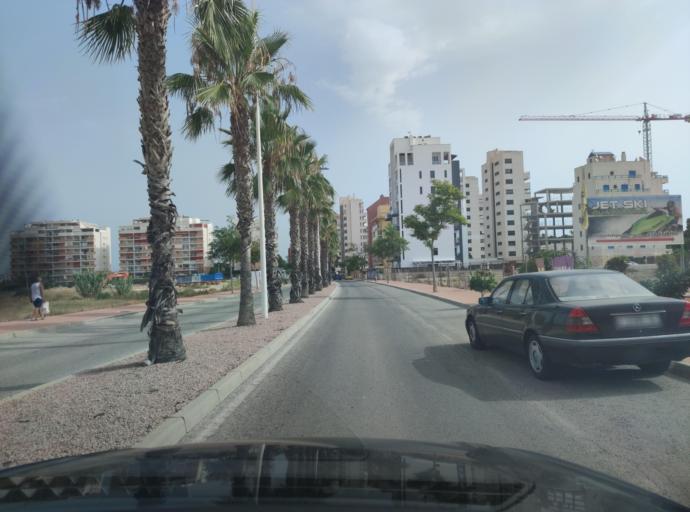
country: ES
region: Valencia
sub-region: Provincia de Alicante
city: Guardamar del Segura
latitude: 38.0982
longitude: -0.6559
